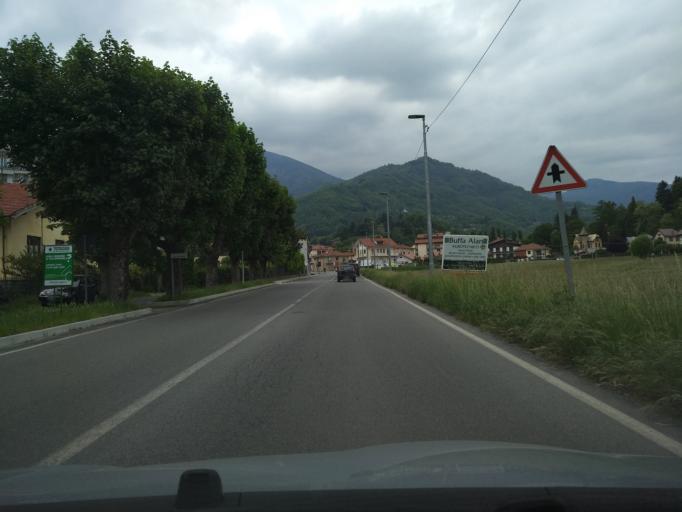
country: IT
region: Piedmont
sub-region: Provincia di Torino
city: Luserna
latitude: 44.8191
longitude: 7.2342
